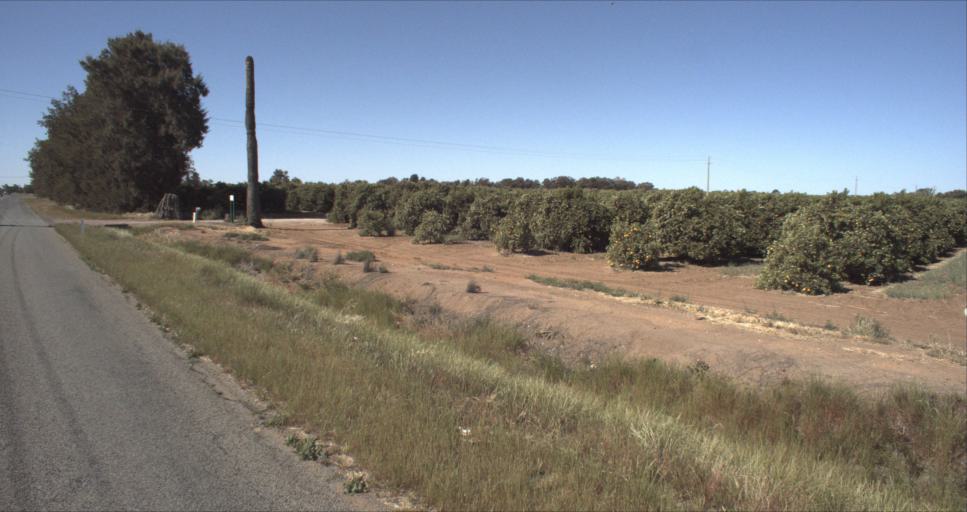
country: AU
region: New South Wales
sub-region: Leeton
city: Leeton
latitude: -34.5673
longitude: 146.3824
